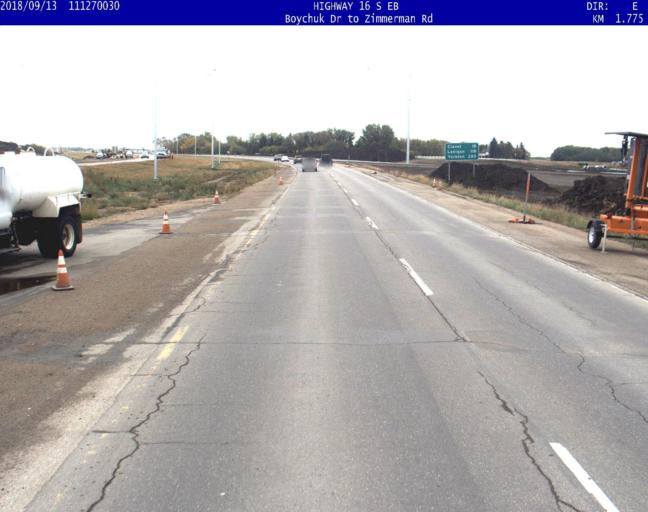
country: CA
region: Saskatchewan
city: Saskatoon
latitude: 52.0868
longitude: -106.5725
